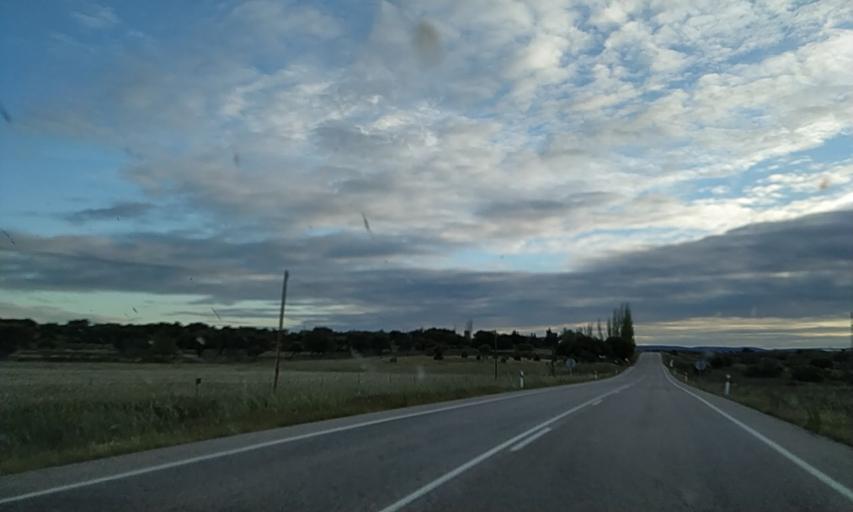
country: ES
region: Extremadura
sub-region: Provincia de Caceres
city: Malpartida de Caceres
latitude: 39.3812
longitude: -6.4452
